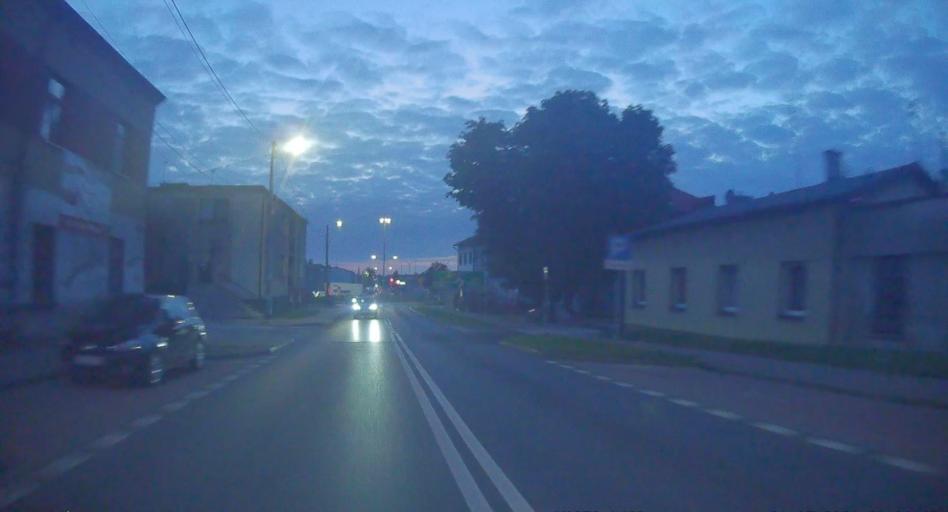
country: PL
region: Silesian Voivodeship
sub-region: Powiat klobucki
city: Klobuck
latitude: 50.9003
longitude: 18.9383
